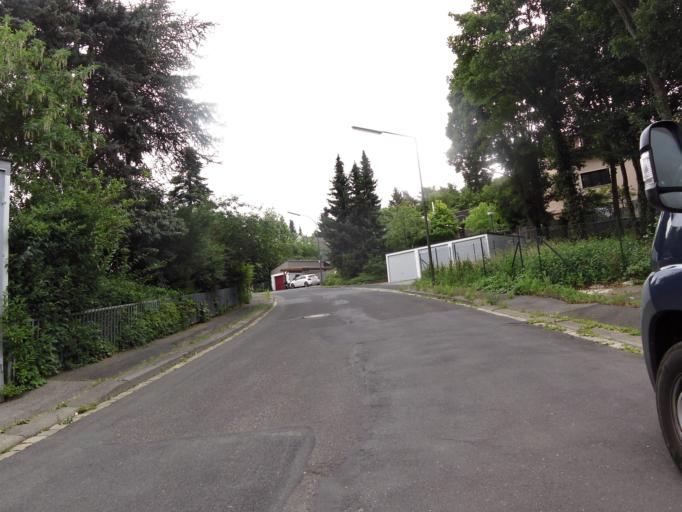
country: DE
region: Bavaria
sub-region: Regierungsbezirk Unterfranken
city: Reichenberg
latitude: 49.7674
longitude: 9.9188
